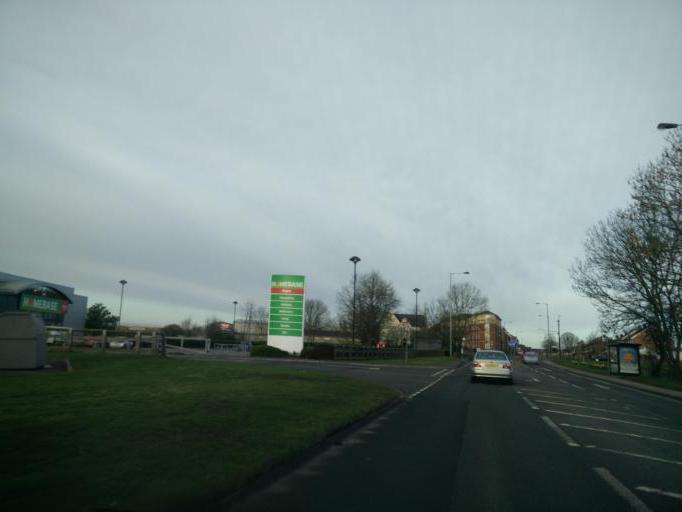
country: GB
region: England
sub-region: County Durham
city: Bishop Auckland
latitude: 54.6424
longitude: -1.6848
